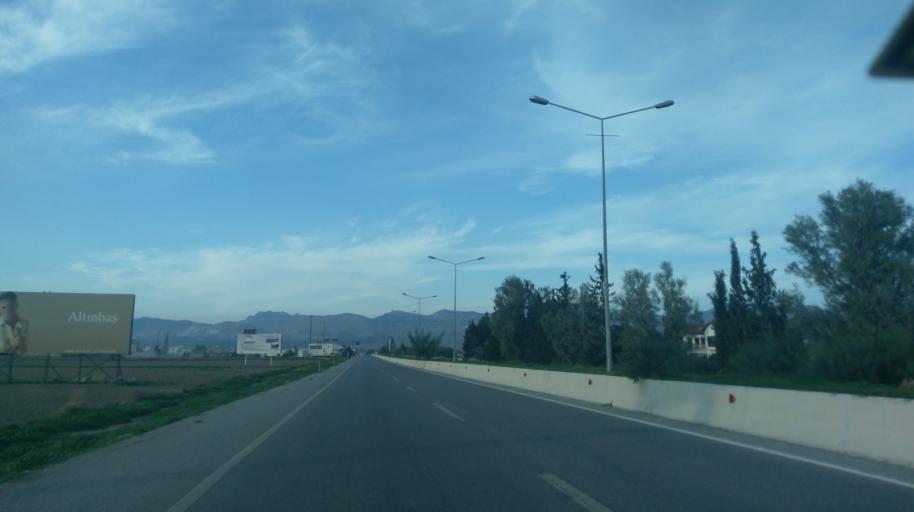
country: CY
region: Lefkosia
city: Geri
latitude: 35.2036
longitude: 33.4995
